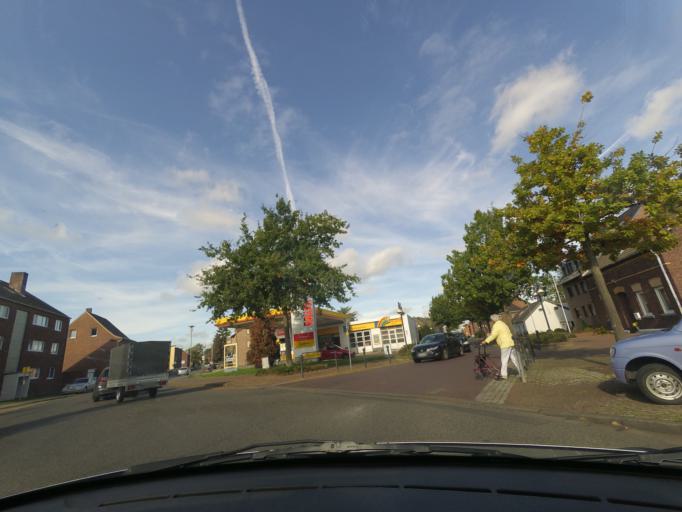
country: DE
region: North Rhine-Westphalia
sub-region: Regierungsbezirk Dusseldorf
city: Korschenbroich
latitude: 51.1920
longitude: 6.5560
